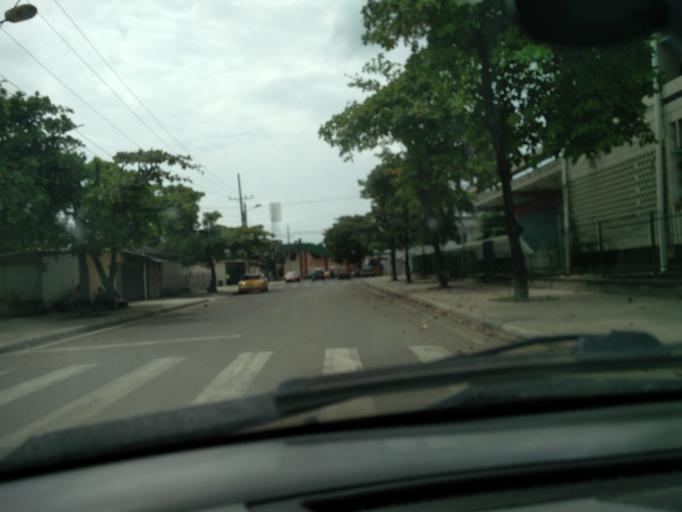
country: EC
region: Manabi
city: Portoviejo
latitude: -1.0507
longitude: -80.4530
